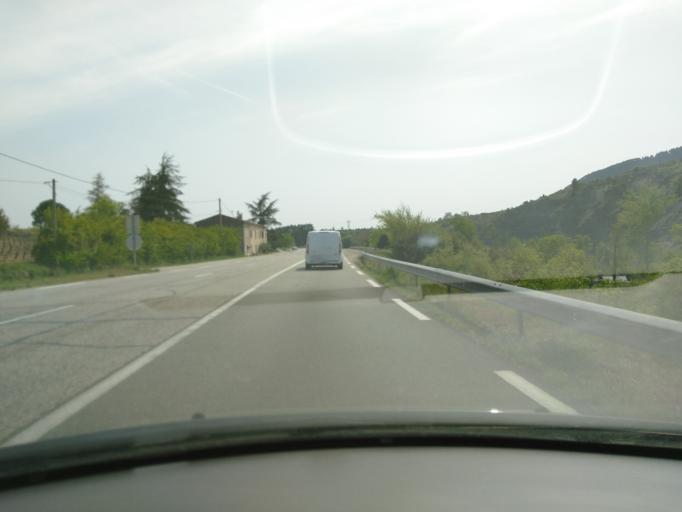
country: FR
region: Rhone-Alpes
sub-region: Departement de l'Ardeche
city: Alba-la-Romaine
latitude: 44.5768
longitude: 4.5782
